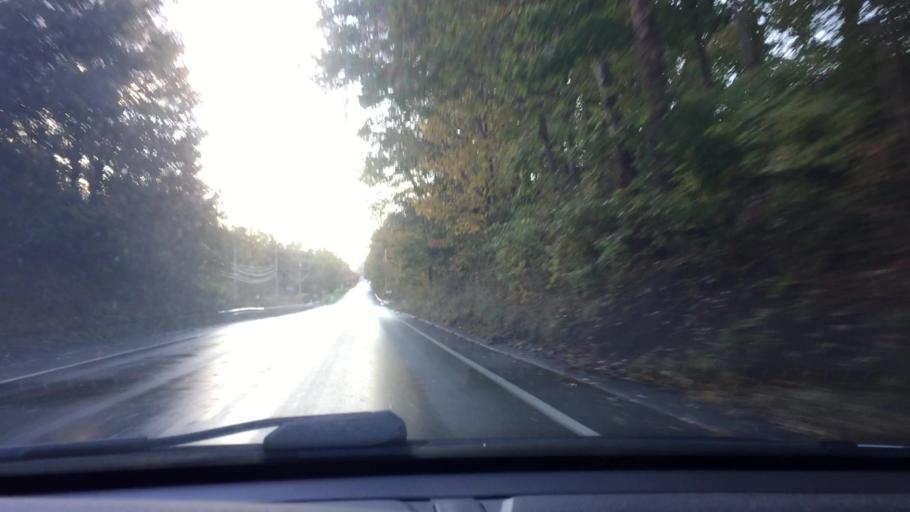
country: US
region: Pennsylvania
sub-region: Lawrence County
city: Bessemer
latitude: 40.9763
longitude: -80.4603
